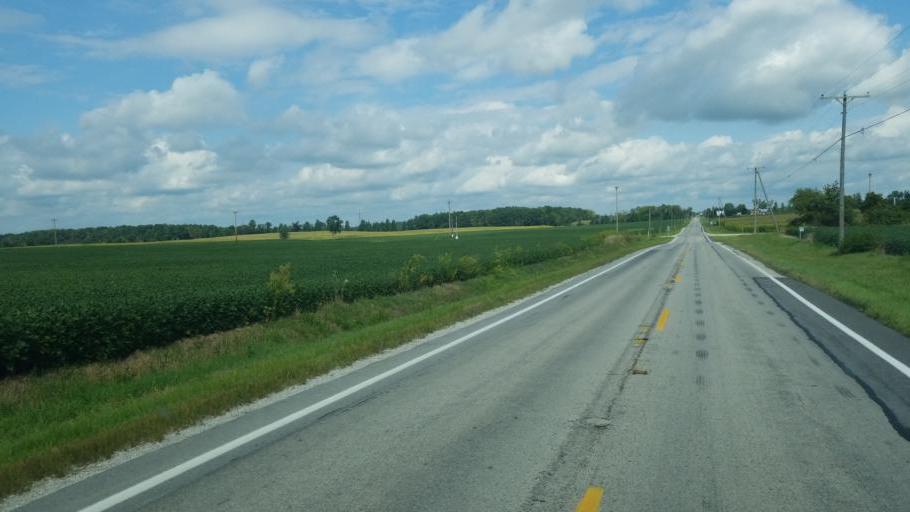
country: US
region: Ohio
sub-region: Seneca County
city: Tiffin
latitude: 41.0940
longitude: -83.0153
